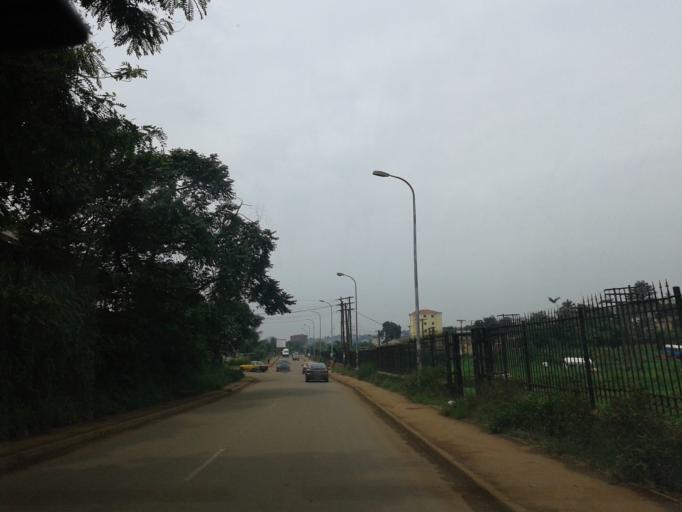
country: CM
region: Centre
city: Yaounde
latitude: 3.8593
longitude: 11.5229
